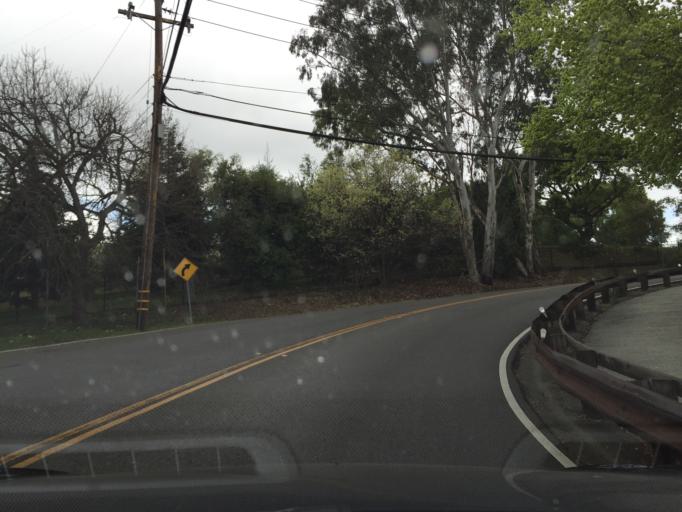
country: US
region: California
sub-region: Santa Clara County
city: Los Altos Hills
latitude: 37.3811
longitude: -122.1261
